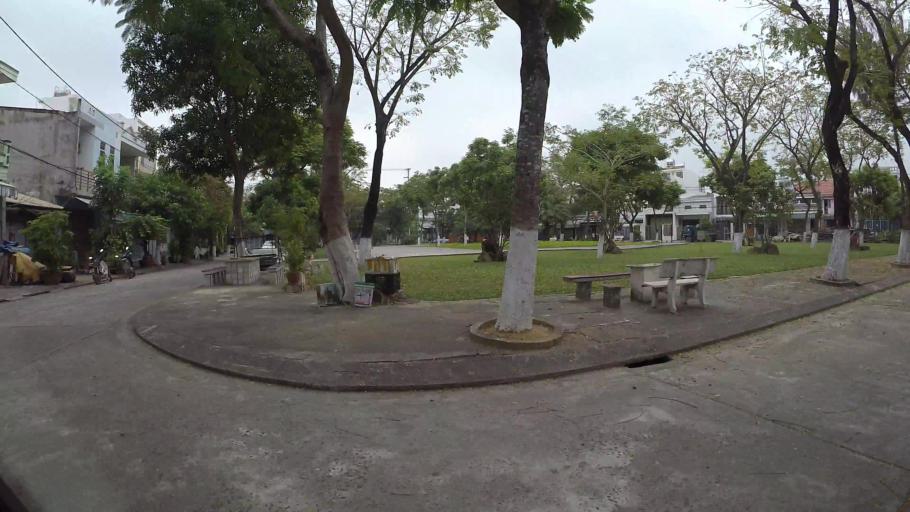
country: VN
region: Da Nang
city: Cam Le
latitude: 16.0281
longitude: 108.2122
